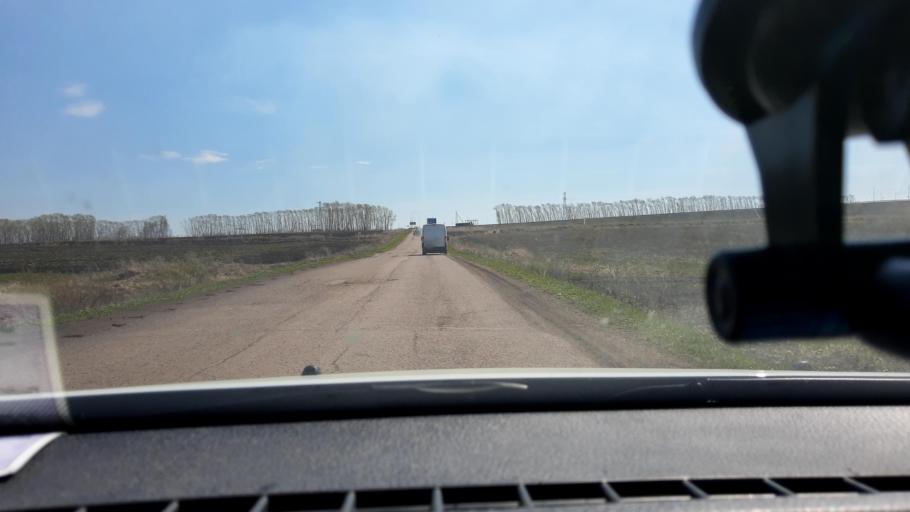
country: RU
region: Bashkortostan
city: Alekseyevka
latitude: 54.7301
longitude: 54.9210
